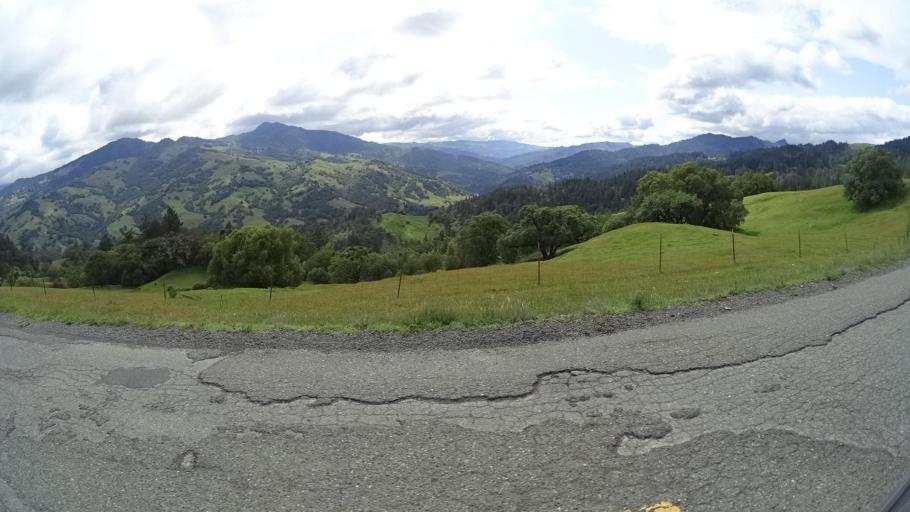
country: US
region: California
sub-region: Humboldt County
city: Redway
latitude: 40.1552
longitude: -123.6226
